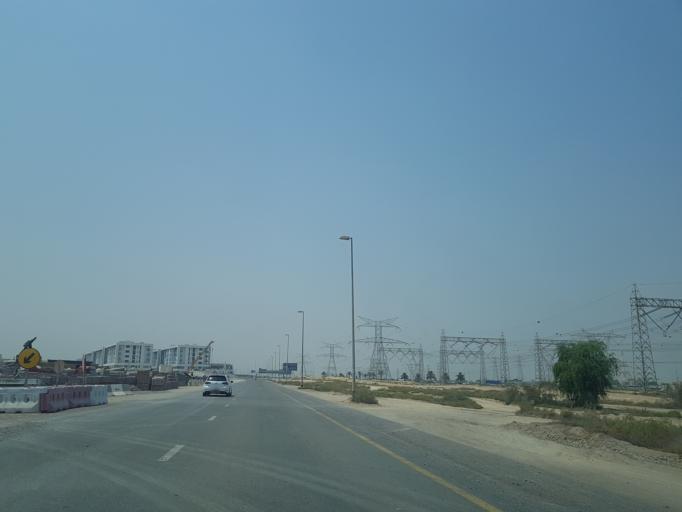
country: AE
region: Ash Shariqah
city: Sharjah
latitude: 25.2250
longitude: 55.4086
